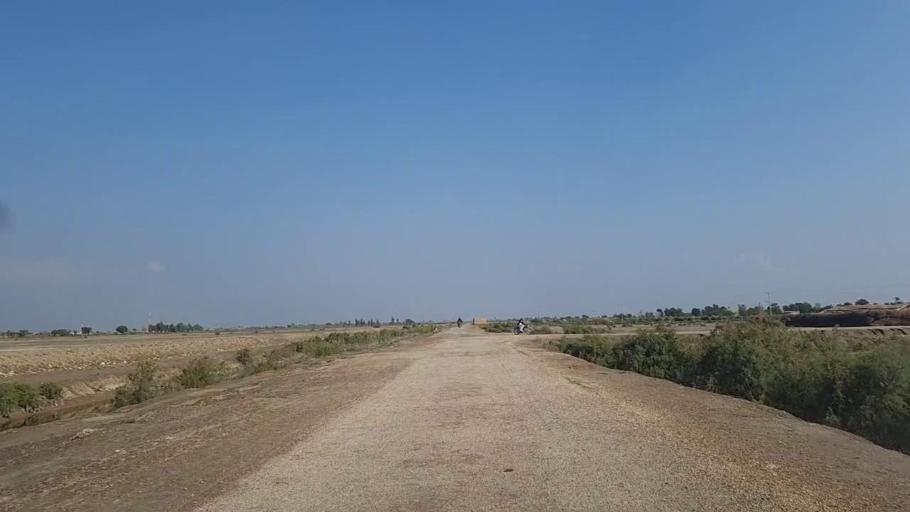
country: PK
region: Sindh
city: Jam Sahib
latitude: 26.2869
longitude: 68.6040
